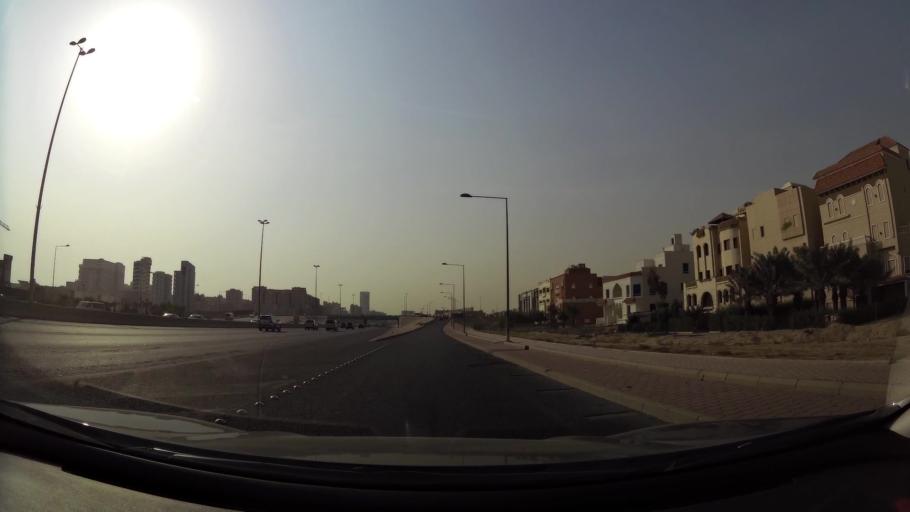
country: KW
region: Al Ahmadi
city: Al Fintas
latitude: 29.1870
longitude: 48.1110
